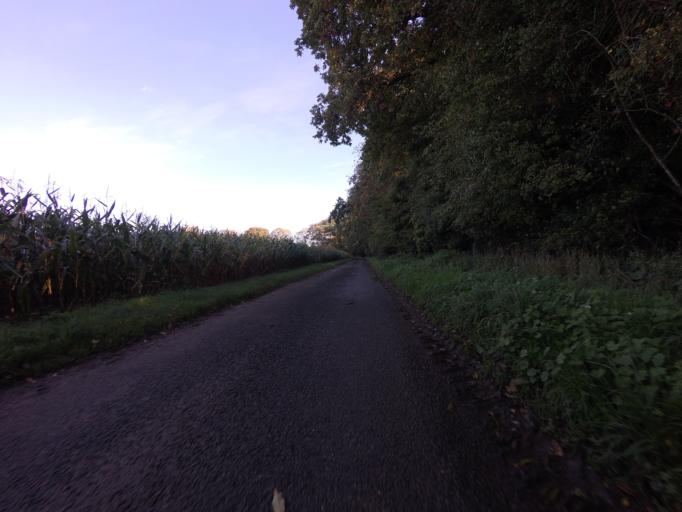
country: GB
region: England
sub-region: Norfolk
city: Dersingham
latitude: 52.8335
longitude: 0.5713
